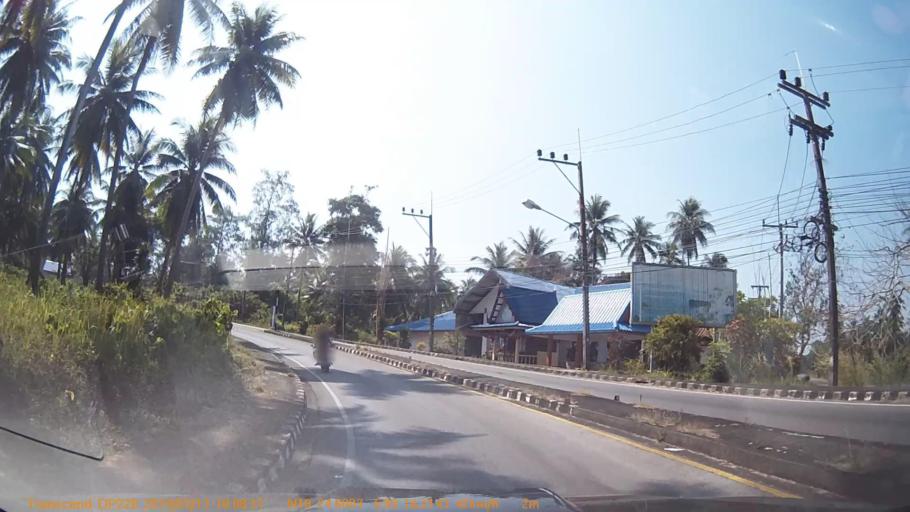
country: TH
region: Chumphon
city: Chumphon
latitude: 10.4099
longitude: 99.2703
